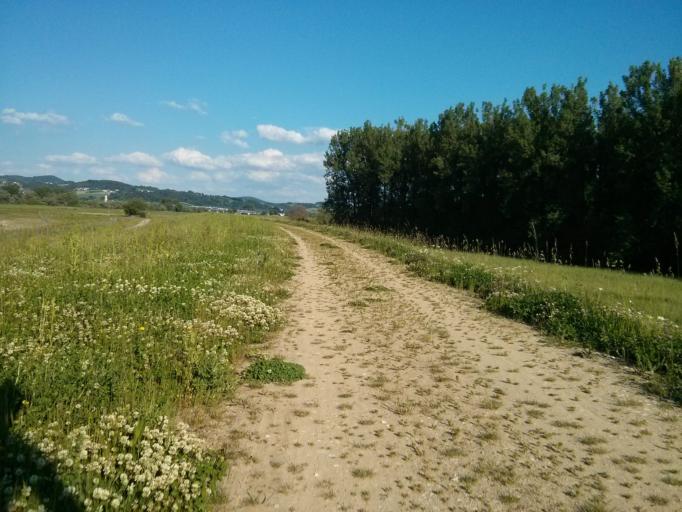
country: DE
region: Bavaria
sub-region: Lower Bavaria
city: Metten
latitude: 48.8332
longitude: 12.9221
